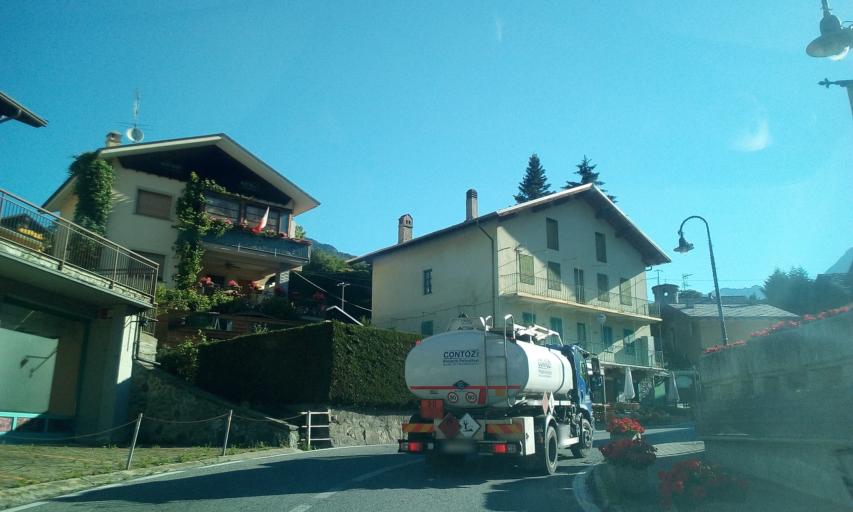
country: IT
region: Aosta Valley
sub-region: Valle d'Aosta
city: Villa-Nabian
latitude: 45.6896
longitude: 7.7059
